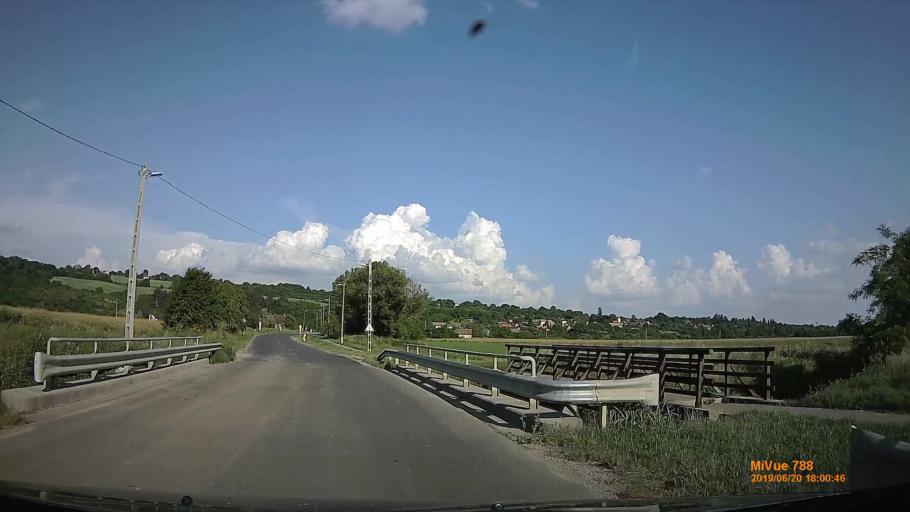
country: HU
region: Baranya
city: Buekkoesd
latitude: 46.0864
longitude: 17.9843
